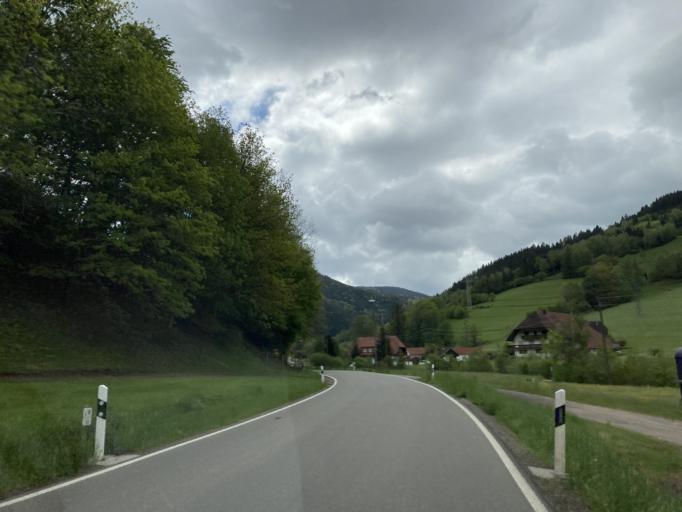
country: DE
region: Baden-Wuerttemberg
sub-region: Freiburg Region
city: Muhlenbach
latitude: 48.2109
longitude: 8.1512
